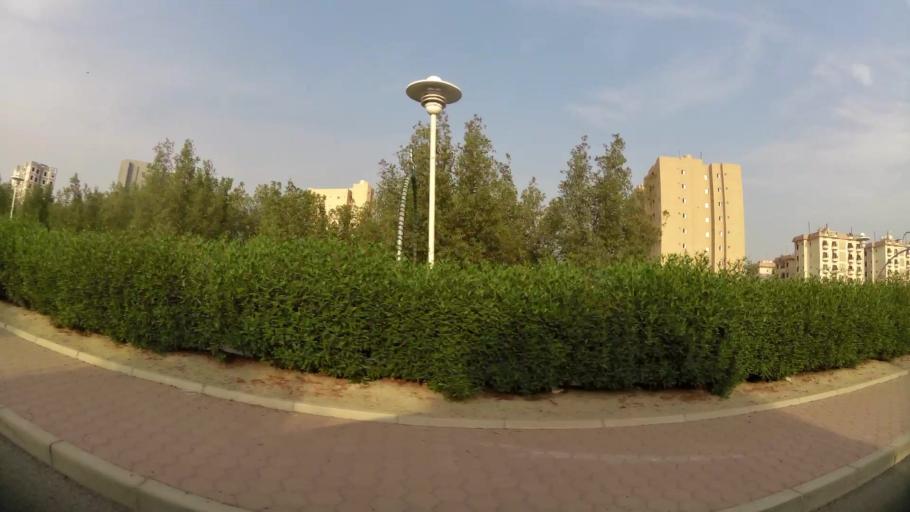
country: KW
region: Mubarak al Kabir
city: Sabah as Salim
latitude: 29.2534
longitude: 48.0792
